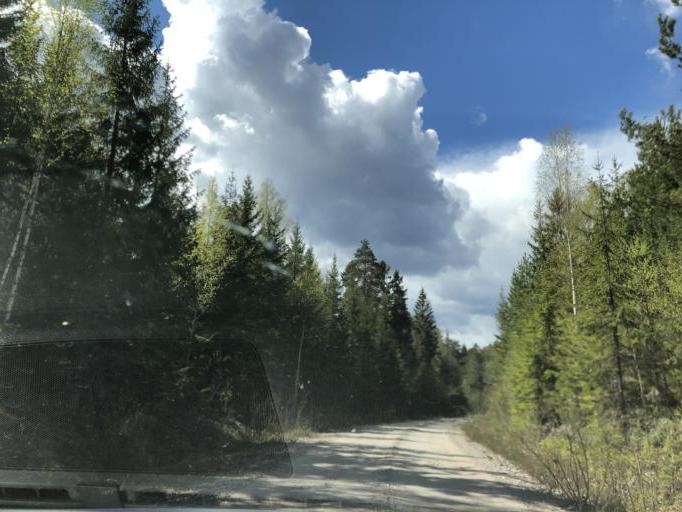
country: SE
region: Uppsala
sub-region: Heby Kommun
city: Tarnsjo
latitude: 60.2394
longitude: 16.8998
